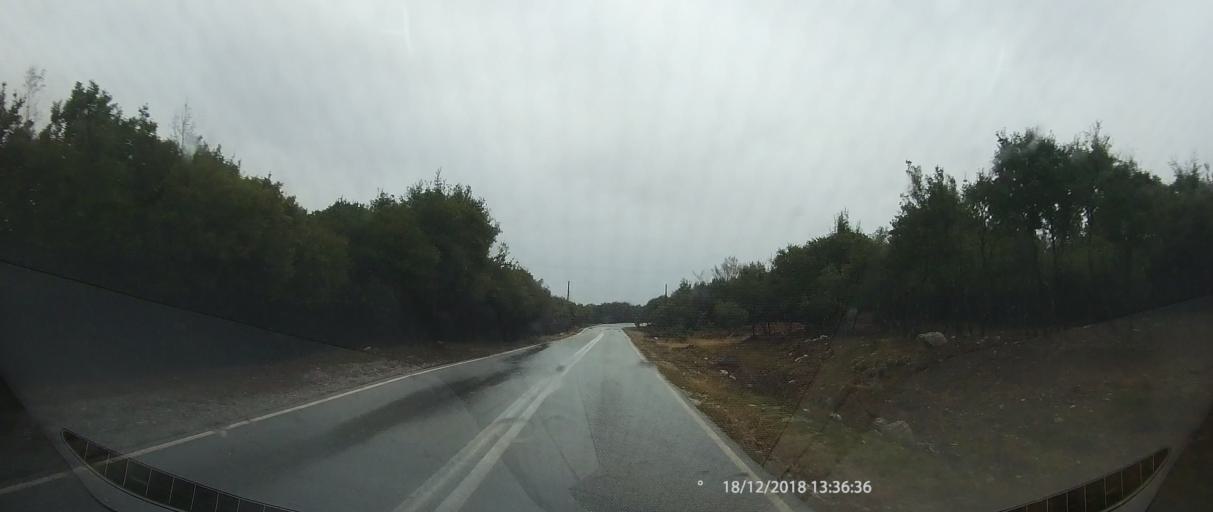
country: GR
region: Central Macedonia
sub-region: Nomos Pierias
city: Litochoro
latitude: 40.1102
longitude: 22.4948
